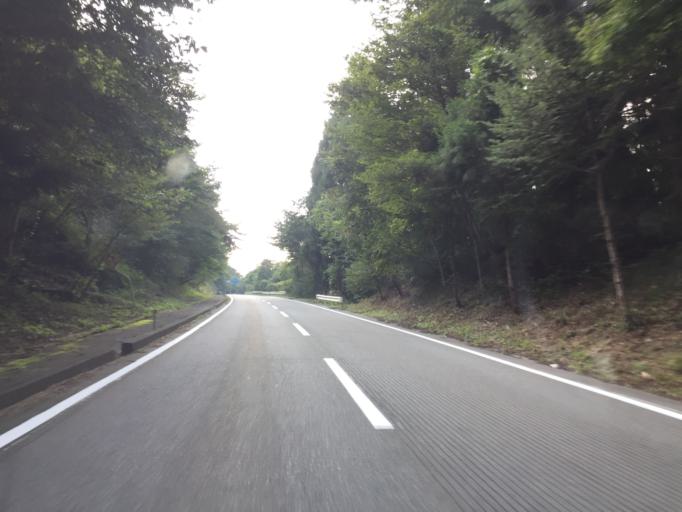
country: JP
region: Fukushima
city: Namie
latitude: 37.5081
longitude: 140.8996
